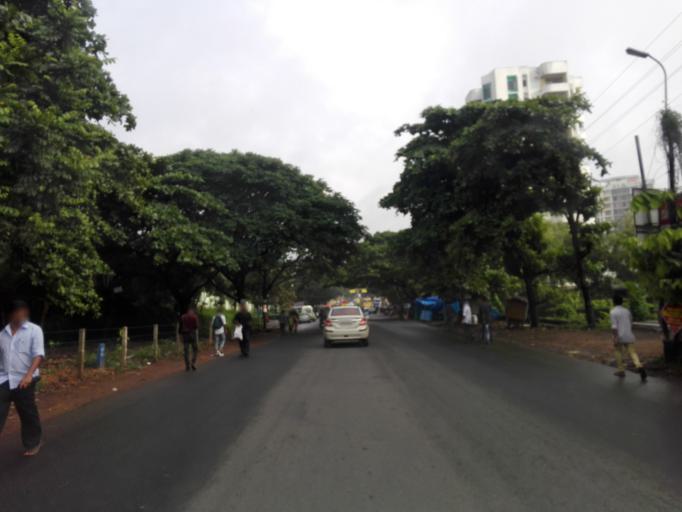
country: IN
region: Kerala
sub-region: Ernakulam
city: Elur
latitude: 10.0052
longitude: 76.3459
